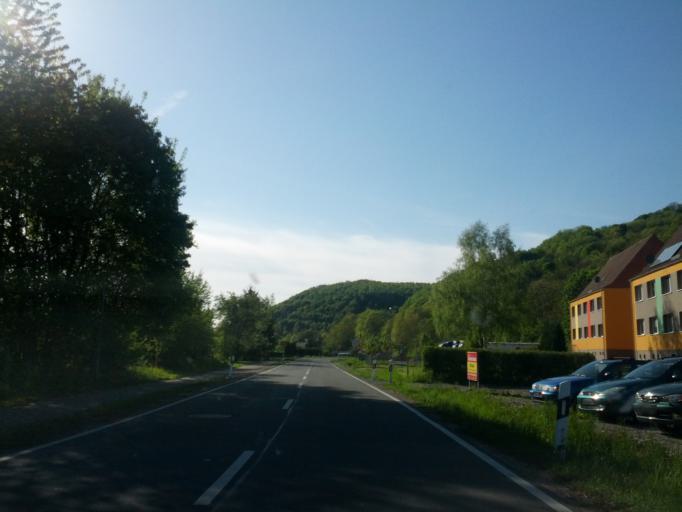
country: DE
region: Thuringia
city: Grossbartloff
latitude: 51.2163
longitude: 10.2131
